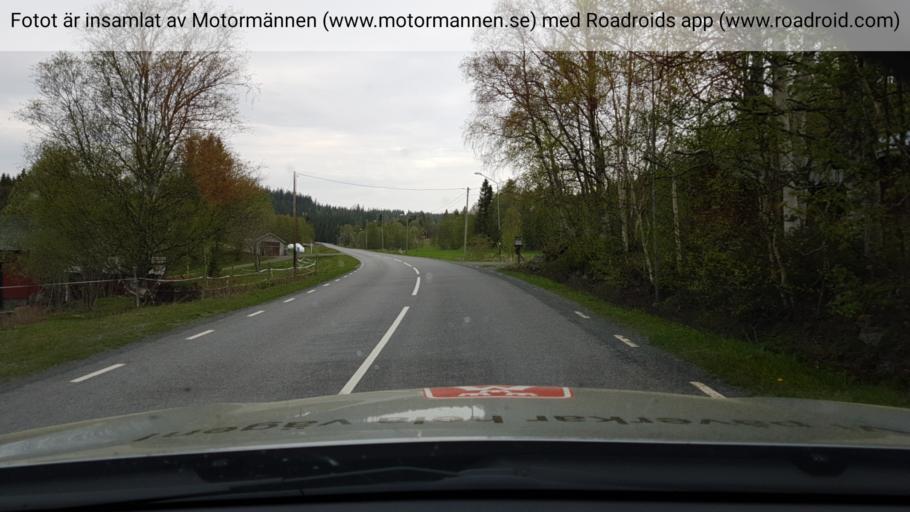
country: SE
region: Jaemtland
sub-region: Are Kommun
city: Are
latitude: 63.5274
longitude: 13.1041
